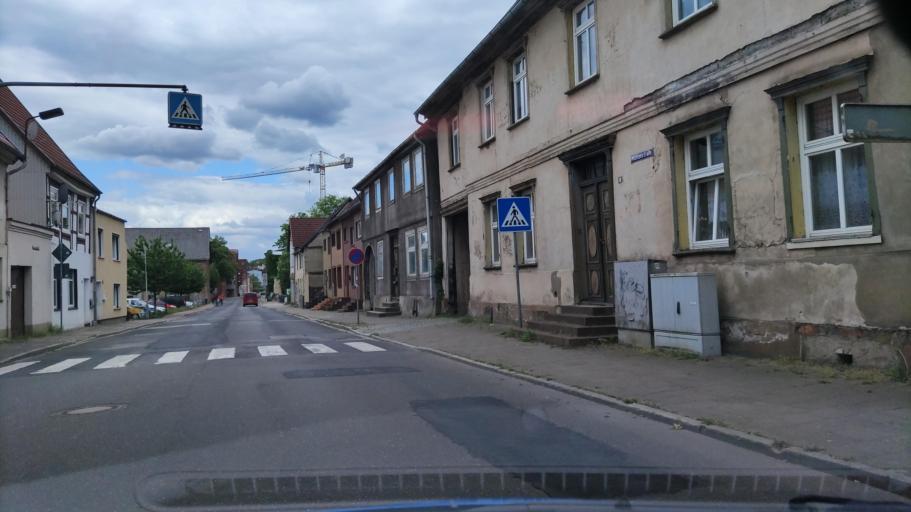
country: DE
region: Mecklenburg-Vorpommern
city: Parchim
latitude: 53.4277
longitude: 11.8408
